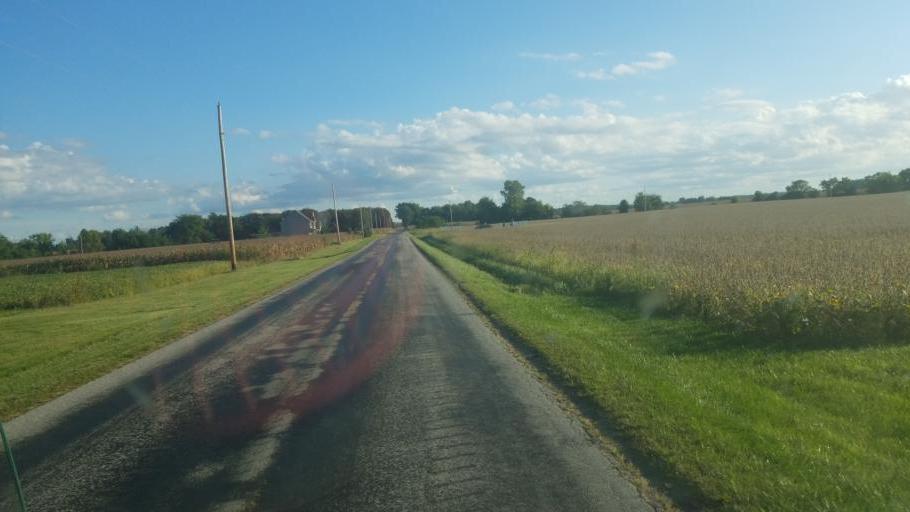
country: US
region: Ohio
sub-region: Wyandot County
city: Carey
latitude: 40.9223
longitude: -83.4009
